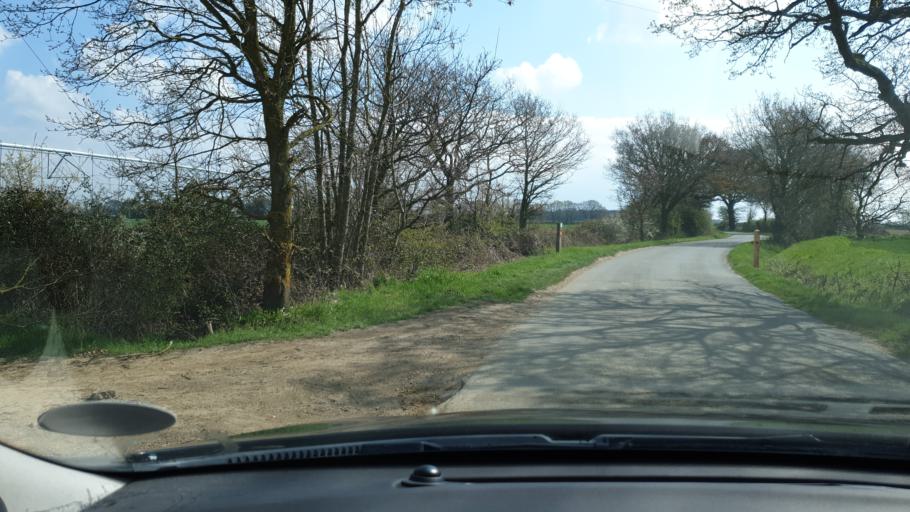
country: GB
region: England
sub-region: Essex
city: Great Bentley
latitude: 51.8409
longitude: 1.0801
